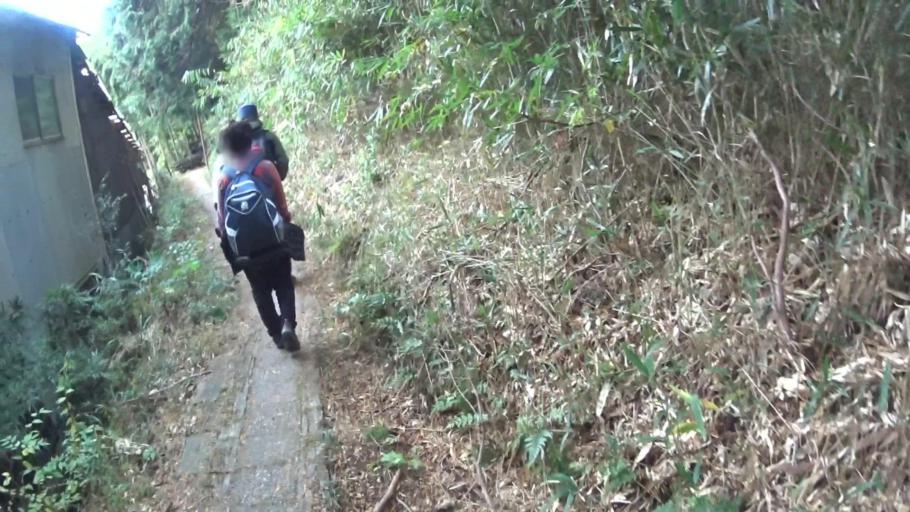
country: JP
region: Kyoto
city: Kyoto
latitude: 34.9650
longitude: 135.7818
